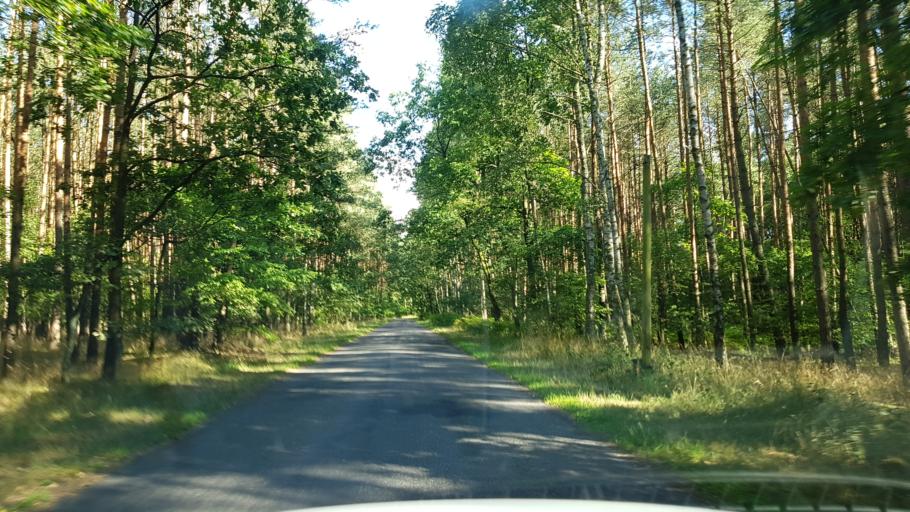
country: PL
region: West Pomeranian Voivodeship
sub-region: Powiat goleniowski
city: Goleniow
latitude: 53.5552
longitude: 14.7685
